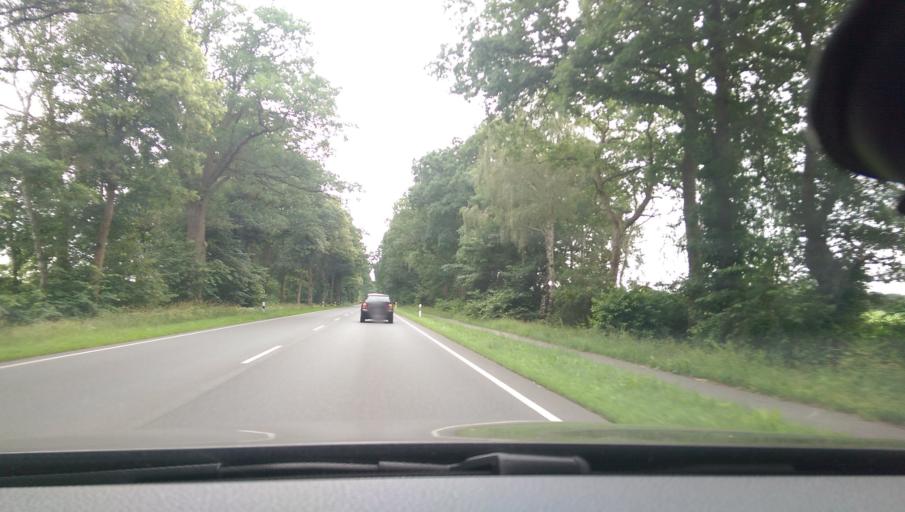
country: DE
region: Lower Saxony
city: Rotenburg
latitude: 53.0874
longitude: 9.3646
